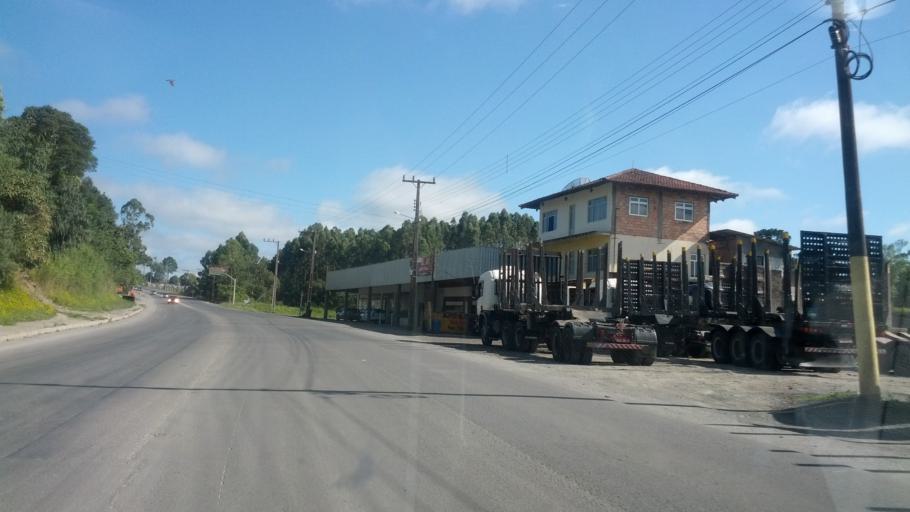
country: BR
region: Santa Catarina
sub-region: Otacilio Costa
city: Otacilio Costa
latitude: -27.4864
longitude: -50.1173
